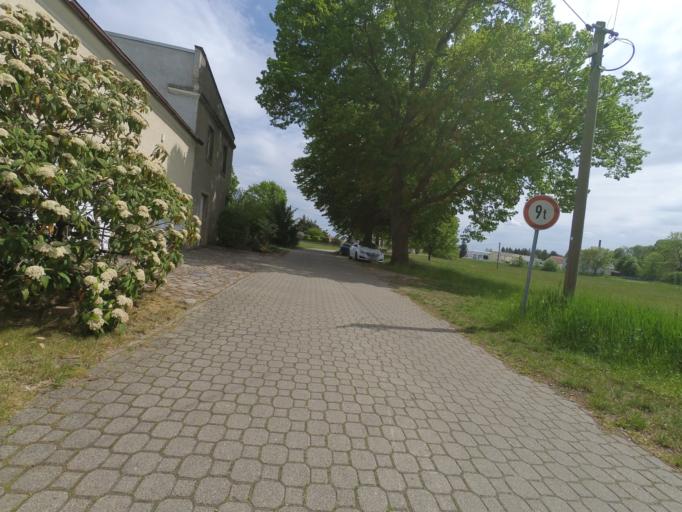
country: DE
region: Saxony
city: Strehla
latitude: 51.3534
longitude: 13.2351
